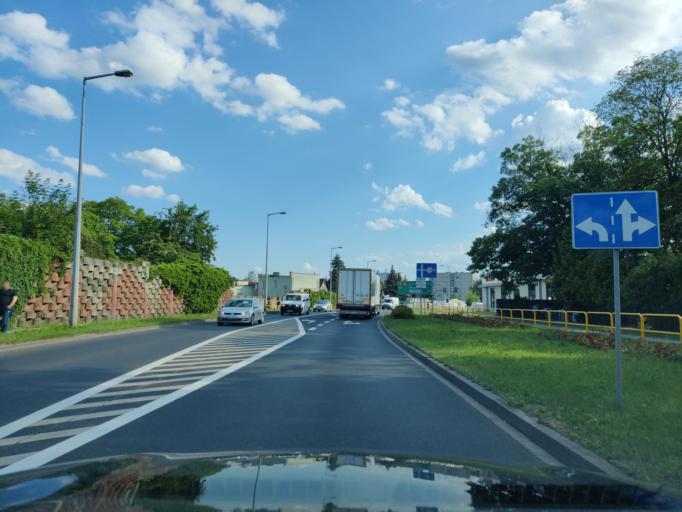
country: PL
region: Greater Poland Voivodeship
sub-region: Powiat wolsztynski
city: Wolsztyn
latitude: 52.1126
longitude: 16.1262
